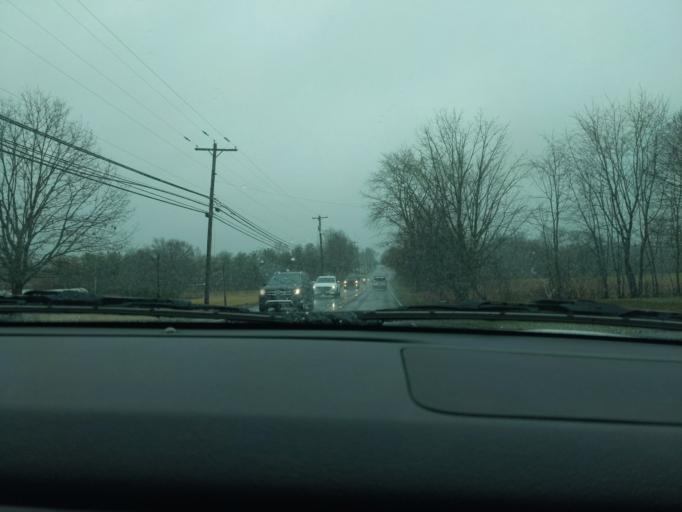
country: US
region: Pennsylvania
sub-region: Bucks County
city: Doylestown
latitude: 40.3436
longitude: -75.1550
